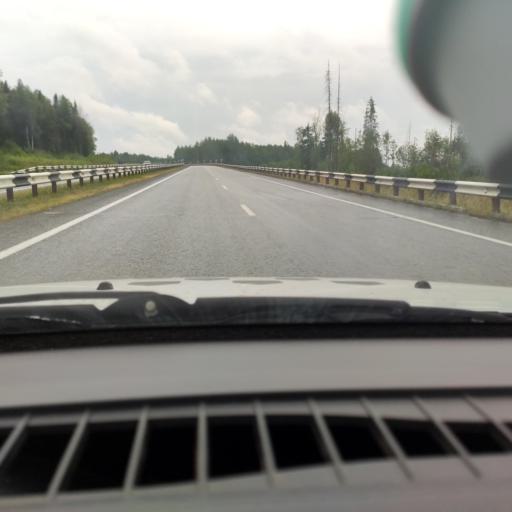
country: RU
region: Perm
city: Polazna
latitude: 58.3308
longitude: 56.4766
